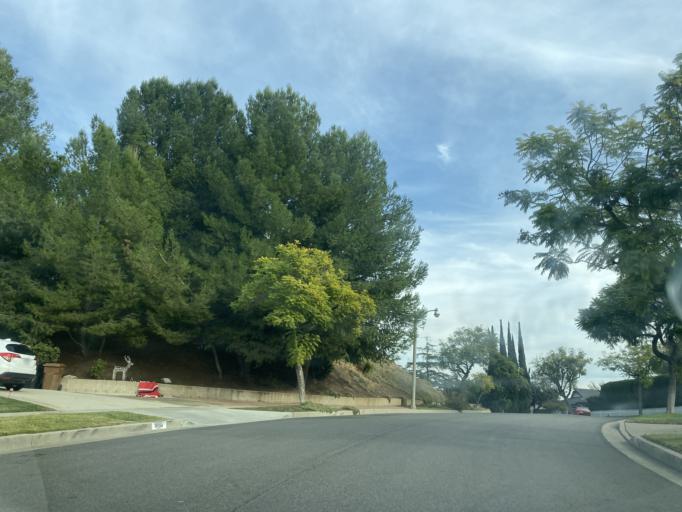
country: US
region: California
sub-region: Orange County
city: Brea
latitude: 33.9026
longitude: -117.8974
